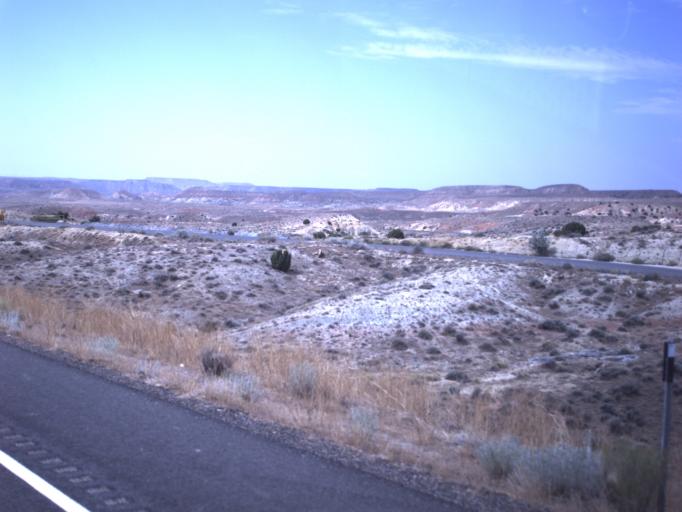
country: US
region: Utah
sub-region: Uintah County
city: Naples
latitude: 40.3342
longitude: -109.4854
